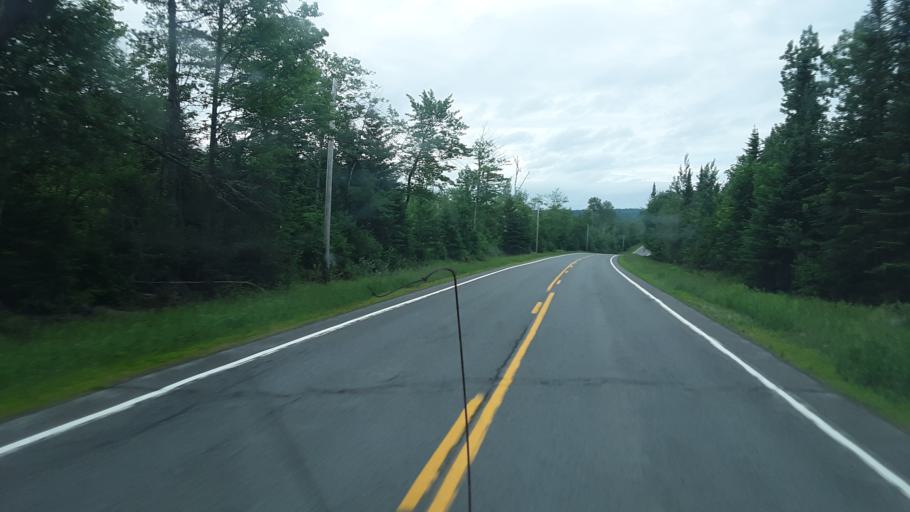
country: US
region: Maine
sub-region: Penobscot County
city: Patten
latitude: 46.3673
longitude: -68.3505
